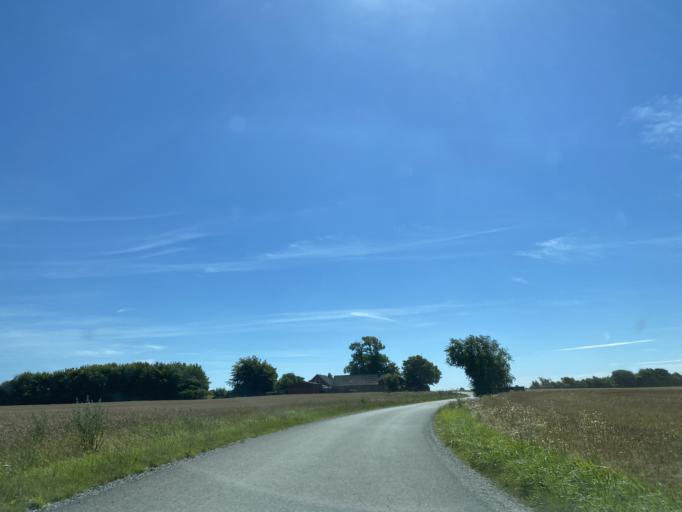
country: DK
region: South Denmark
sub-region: Fredericia Kommune
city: Taulov
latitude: 55.6058
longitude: 9.5377
